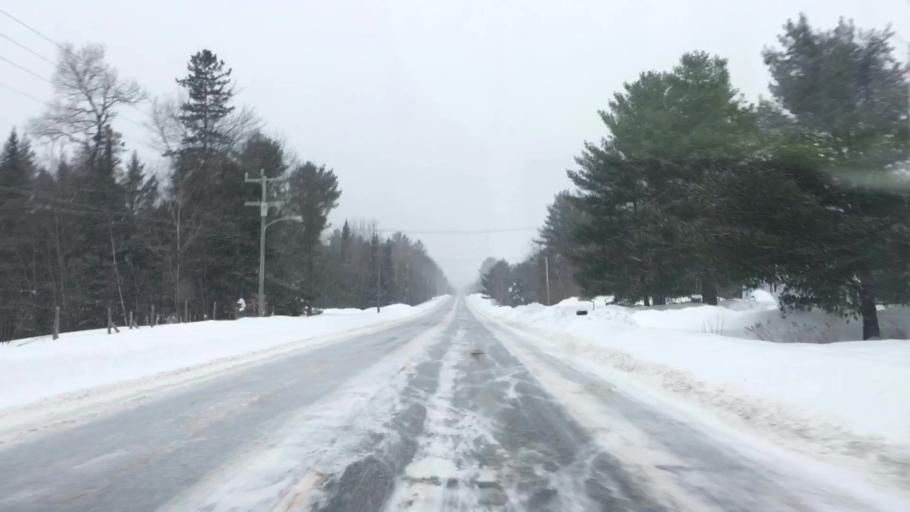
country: US
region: Maine
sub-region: Penobscot County
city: Medway
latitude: 45.5456
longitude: -68.3730
